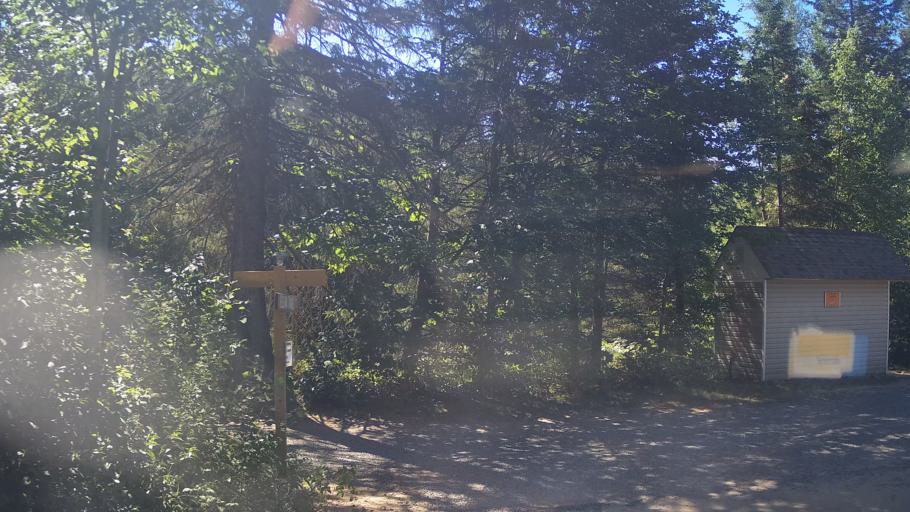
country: CA
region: Ontario
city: Huntsville
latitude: 45.3771
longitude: -79.2148
